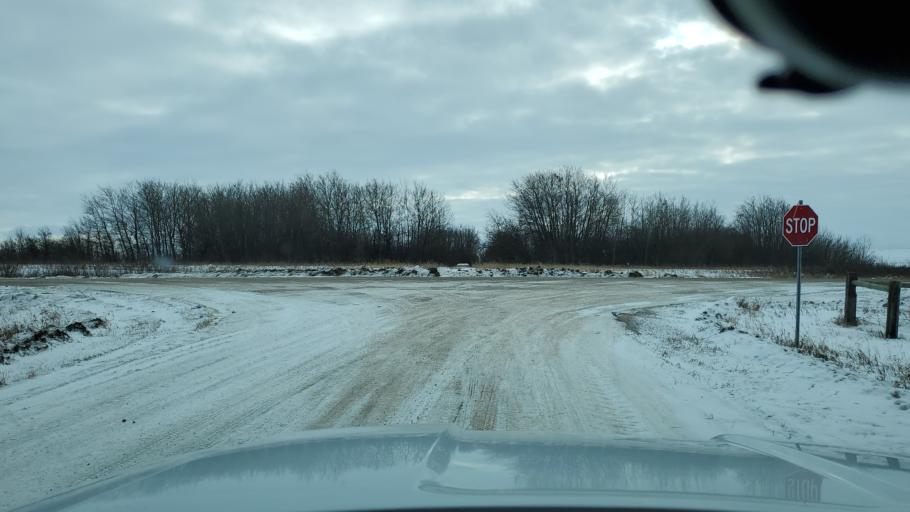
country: CA
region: Saskatchewan
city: White City
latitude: 50.7470
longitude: -104.1545
